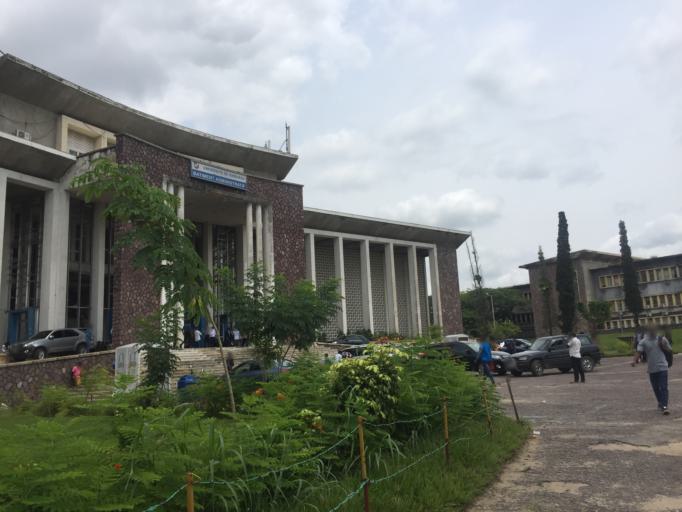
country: CD
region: Kinshasa
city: Masina
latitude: -4.4193
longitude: 15.3089
